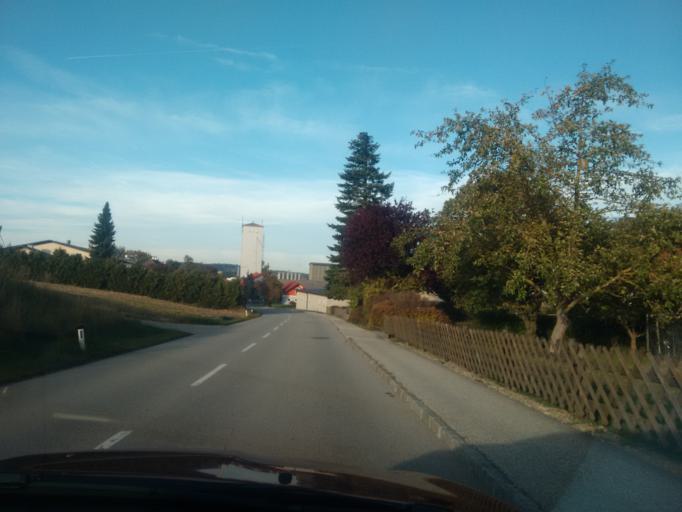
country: AT
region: Upper Austria
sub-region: Politischer Bezirk Vocklabruck
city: Niederthalheim
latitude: 48.1332
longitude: 13.7266
